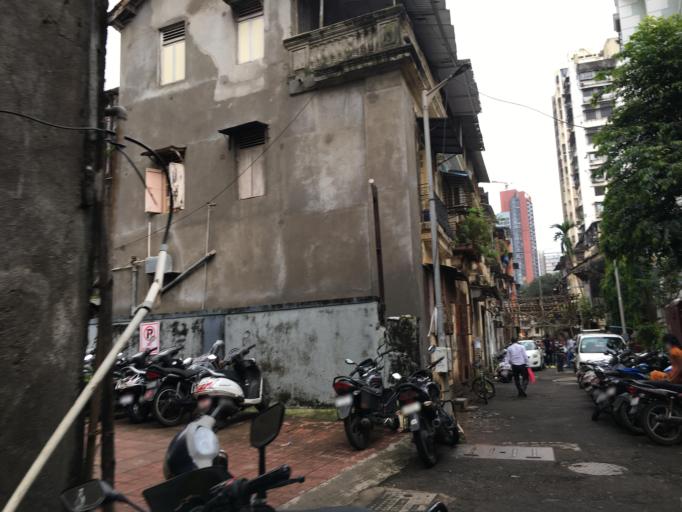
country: IN
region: Maharashtra
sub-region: Mumbai Suburban
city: Mumbai
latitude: 18.9508
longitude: 72.8249
